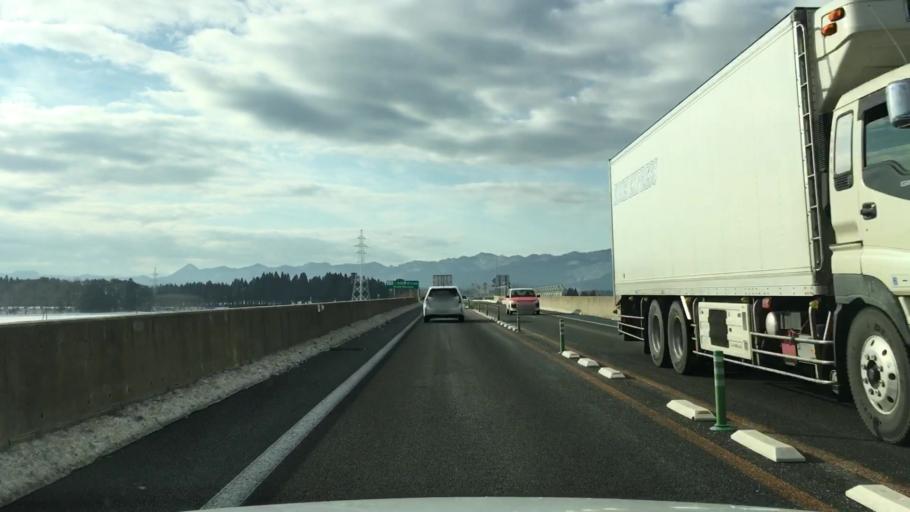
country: JP
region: Akita
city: Odate
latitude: 40.2647
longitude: 140.5259
